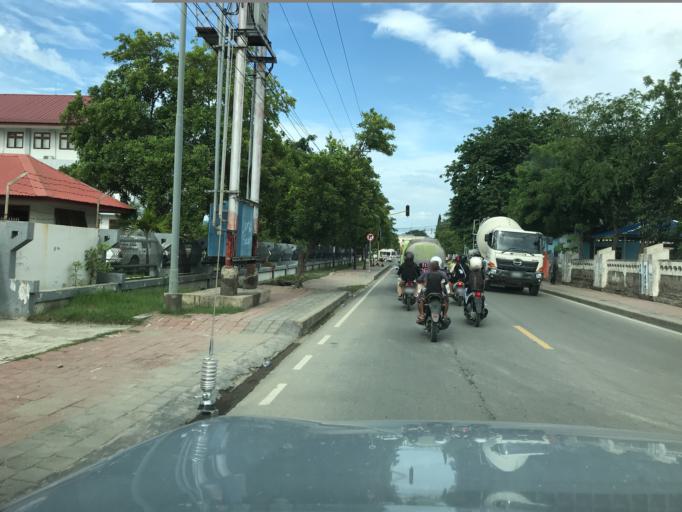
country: TL
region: Dili
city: Dili
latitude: -8.5572
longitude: 125.5681
